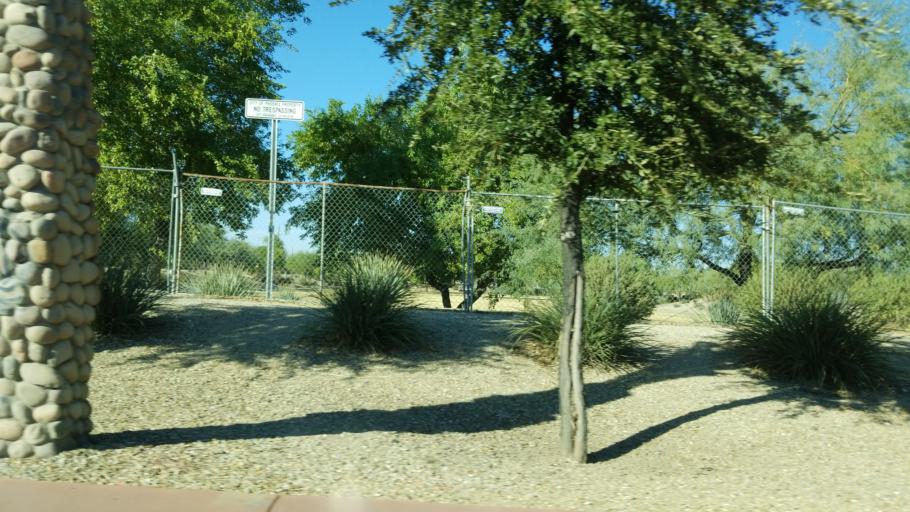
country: US
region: Arizona
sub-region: Maricopa County
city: Phoenix
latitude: 33.5097
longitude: -112.1101
